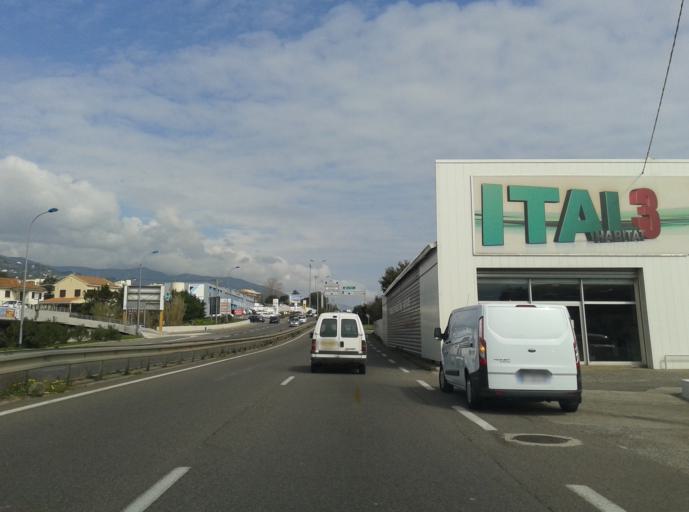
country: FR
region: Corsica
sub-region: Departement de la Haute-Corse
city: Furiani
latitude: 42.6656
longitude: 9.4428
